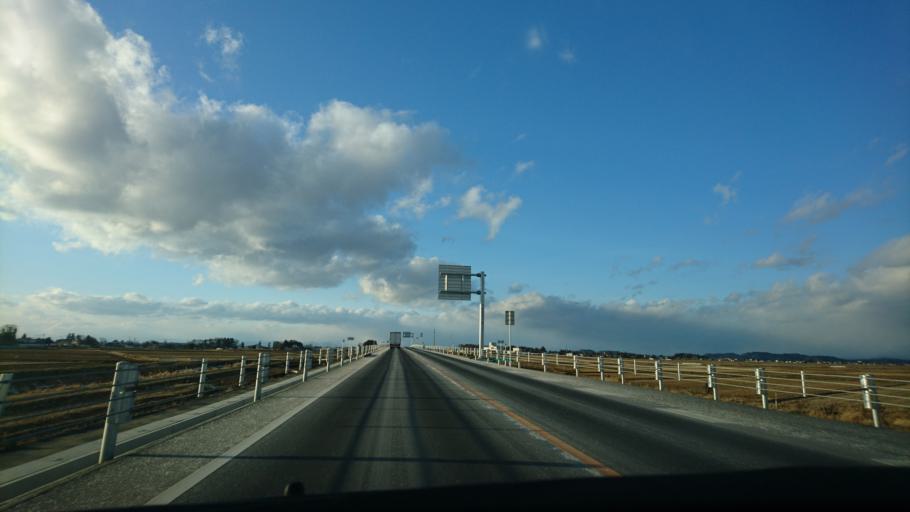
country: JP
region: Miyagi
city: Wakuya
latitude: 38.6789
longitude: 141.2581
